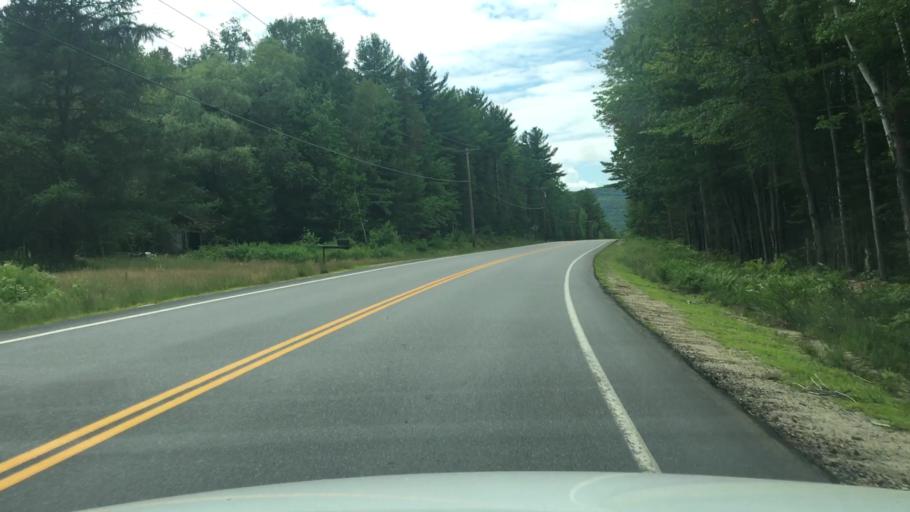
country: US
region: Maine
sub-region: Oxford County
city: West Paris
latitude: 44.3655
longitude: -70.4884
